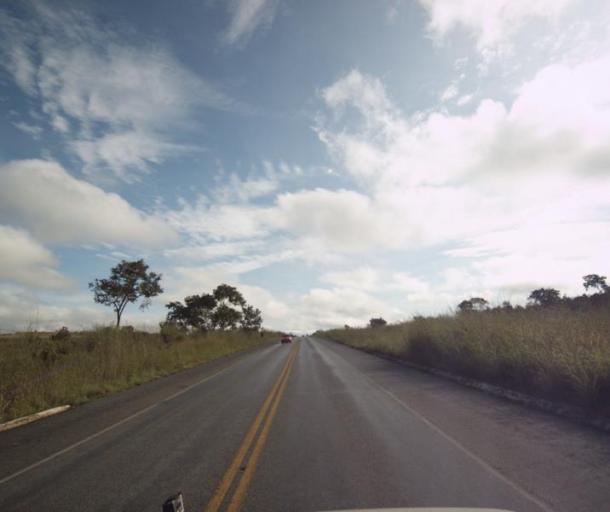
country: BR
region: Goias
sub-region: Padre Bernardo
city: Padre Bernardo
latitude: -15.4812
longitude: -48.6162
